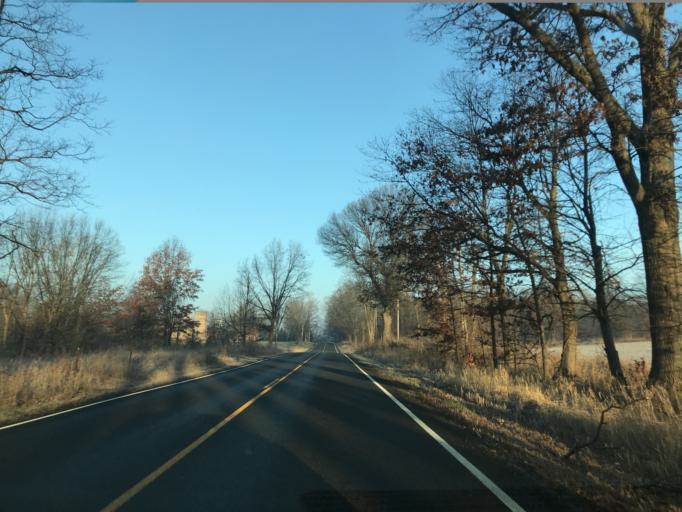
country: US
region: Michigan
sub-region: Ingham County
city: Leslie
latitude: 42.3814
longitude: -84.4507
